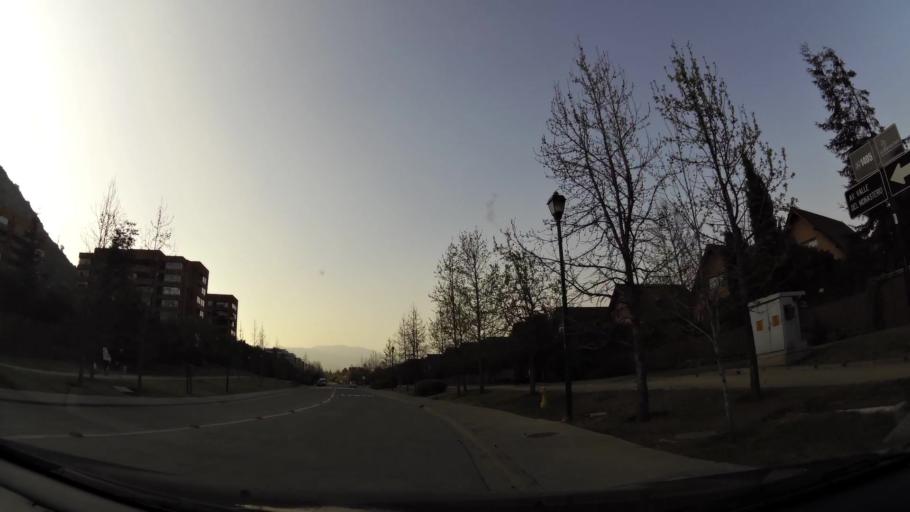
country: CL
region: Santiago Metropolitan
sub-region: Provincia de Santiago
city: Villa Presidente Frei, Nunoa, Santiago, Chile
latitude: -33.3541
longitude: -70.5454
